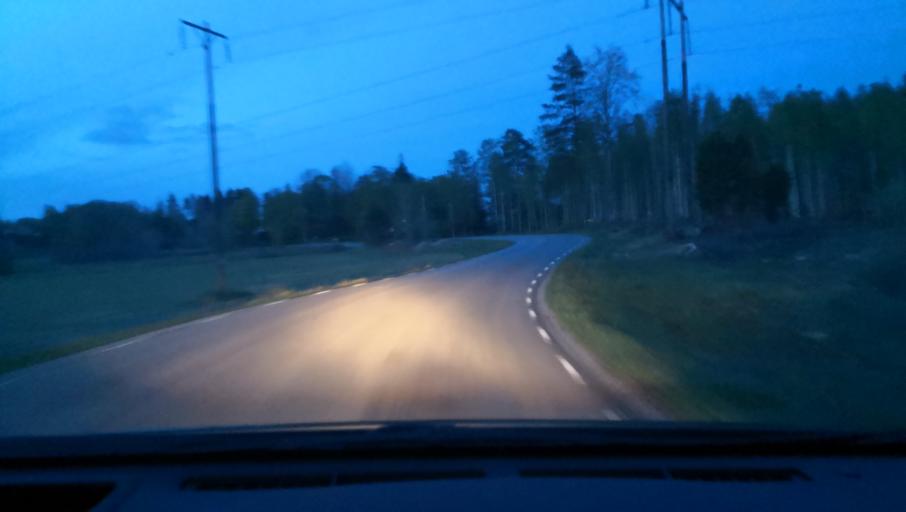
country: SE
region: OErebro
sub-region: Orebro Kommun
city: Vintrosa
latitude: 59.1858
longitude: 15.0379
